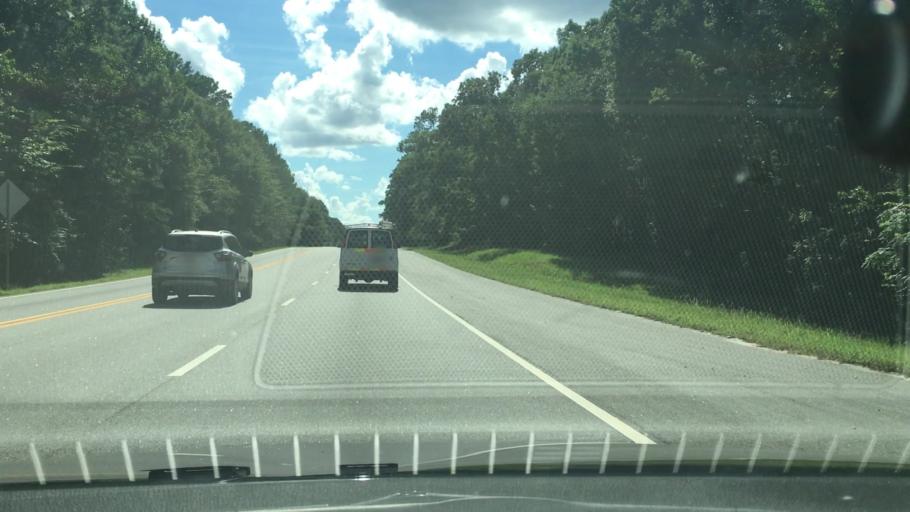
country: US
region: Georgia
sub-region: Butts County
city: Jackson
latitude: 33.2913
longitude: -83.9908
